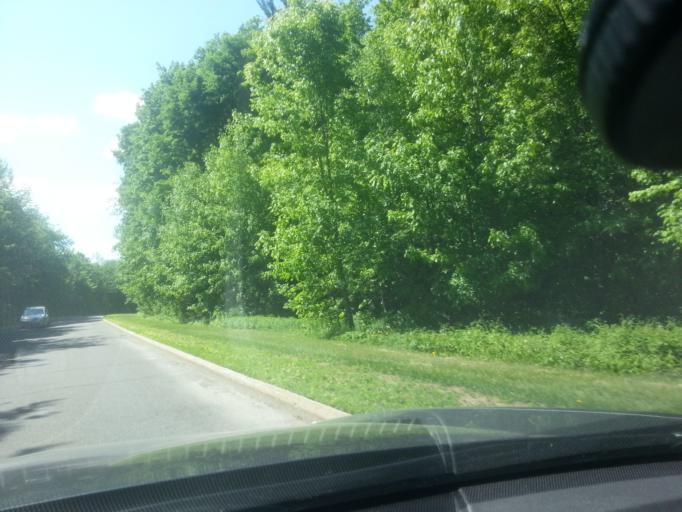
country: CA
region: Ontario
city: Ottawa
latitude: 45.4287
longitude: -75.7476
